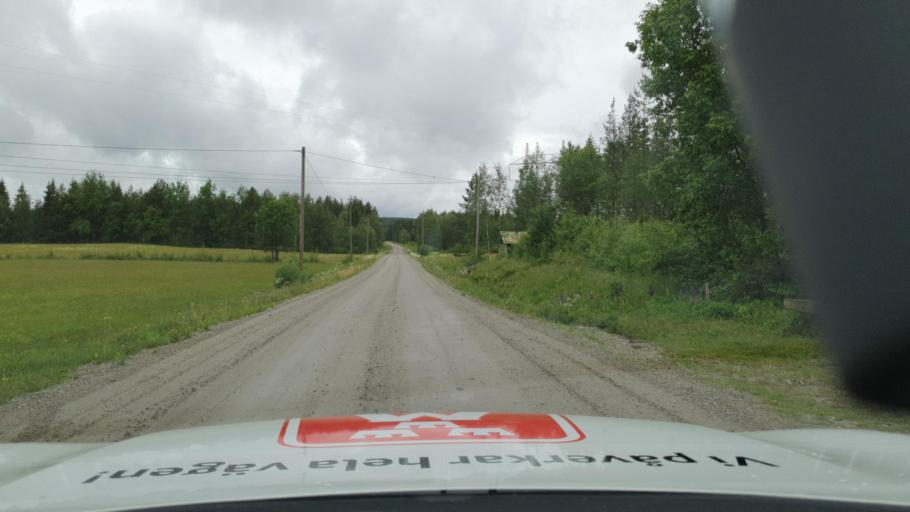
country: SE
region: Vaesterbotten
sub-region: Dorotea Kommun
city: Dorotea
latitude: 64.0190
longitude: 16.7933
